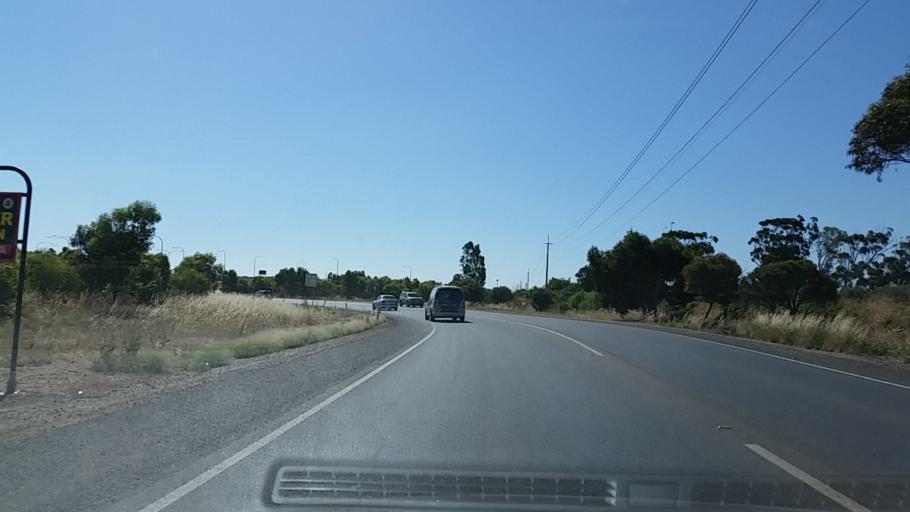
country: AU
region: South Australia
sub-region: Playford
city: Angle Vale
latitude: -34.6635
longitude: 138.6598
